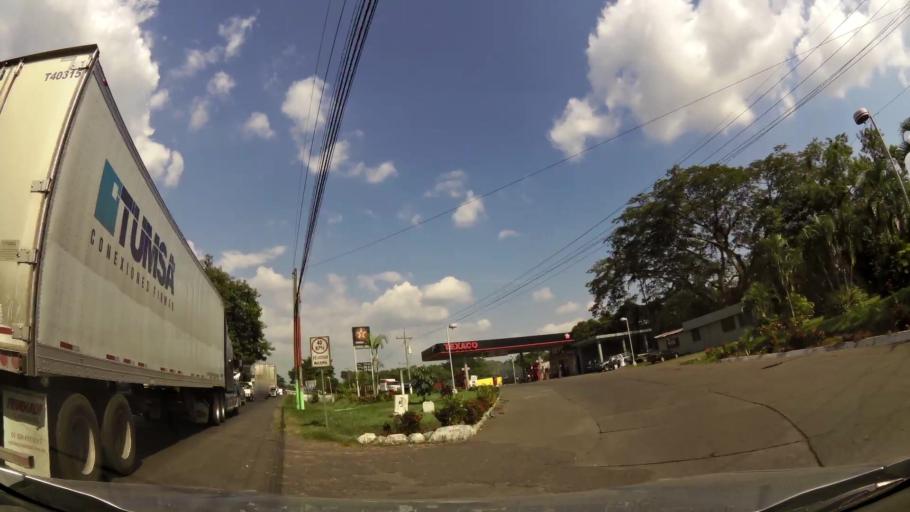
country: GT
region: Suchitepeque
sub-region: Municipio de Cuyotenango
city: Cuyotenango
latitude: 14.5426
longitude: -91.5689
